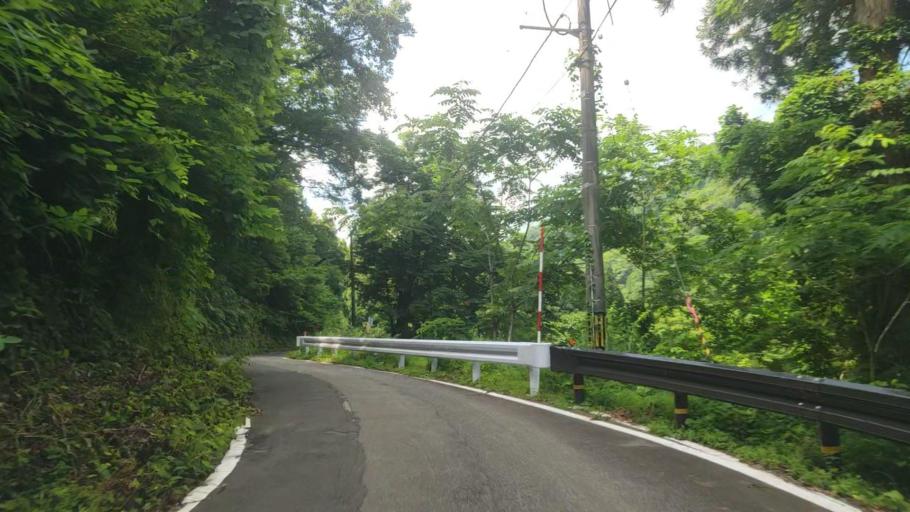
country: JP
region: Fukui
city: Katsuyama
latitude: 36.2163
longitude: 136.5293
